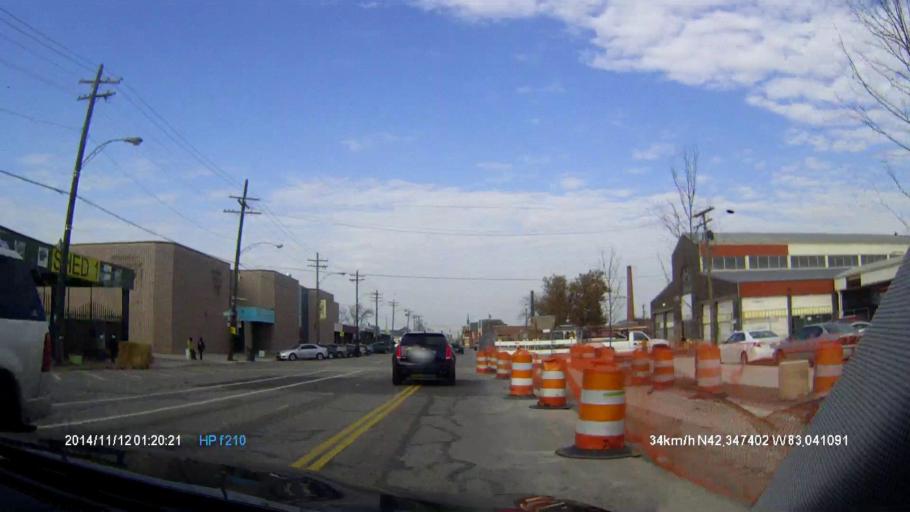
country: US
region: Michigan
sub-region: Wayne County
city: Detroit
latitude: 42.3476
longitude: -83.0412
